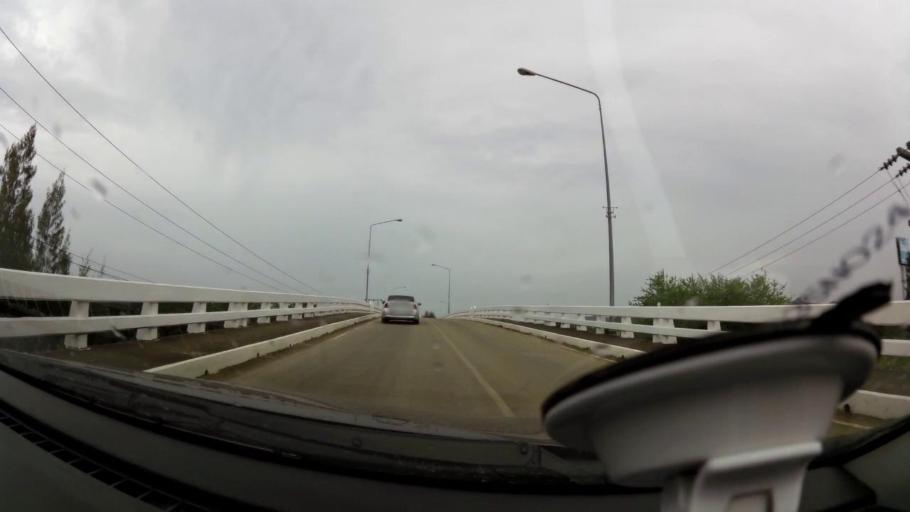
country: TH
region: Prachuap Khiri Khan
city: Pran Buri
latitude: 12.4061
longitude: 99.9676
